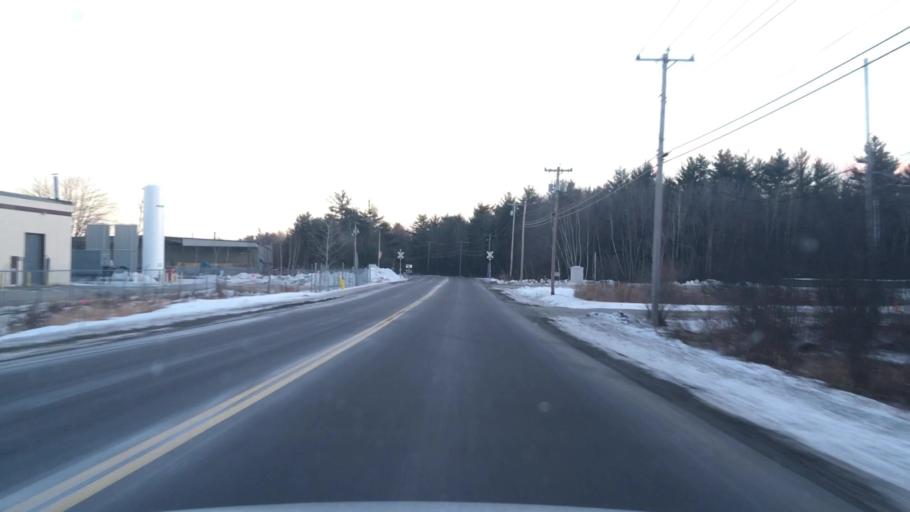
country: US
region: Maine
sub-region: Androscoggin County
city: Auburn
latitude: 44.0730
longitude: -70.2540
